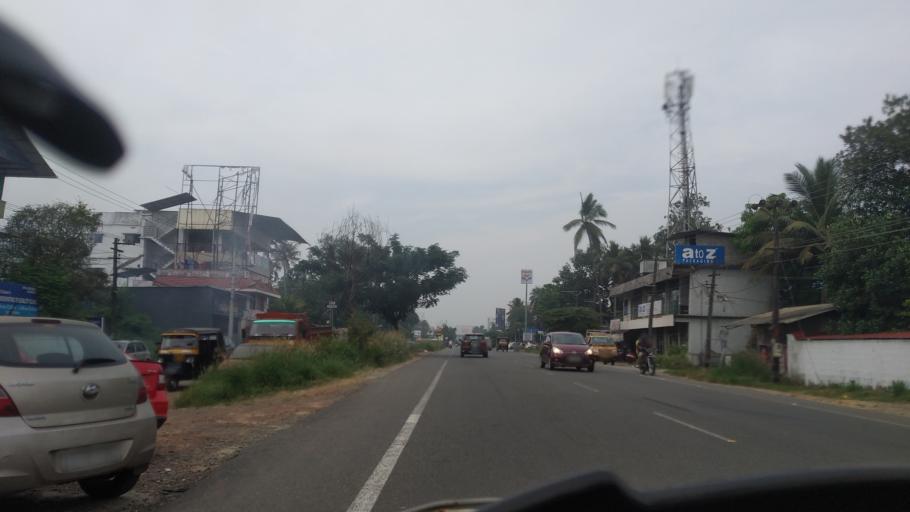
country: IN
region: Kerala
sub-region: Ernakulam
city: Elur
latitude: 10.0527
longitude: 76.2931
